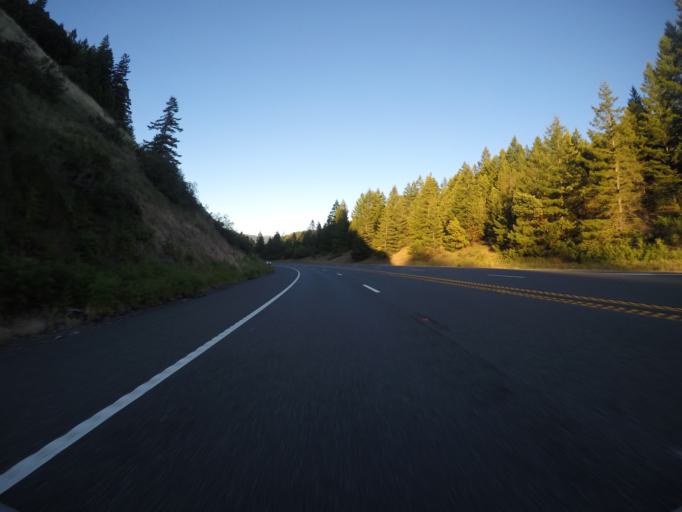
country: US
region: California
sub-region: Mendocino County
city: Laytonville
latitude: 39.8260
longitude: -123.6707
